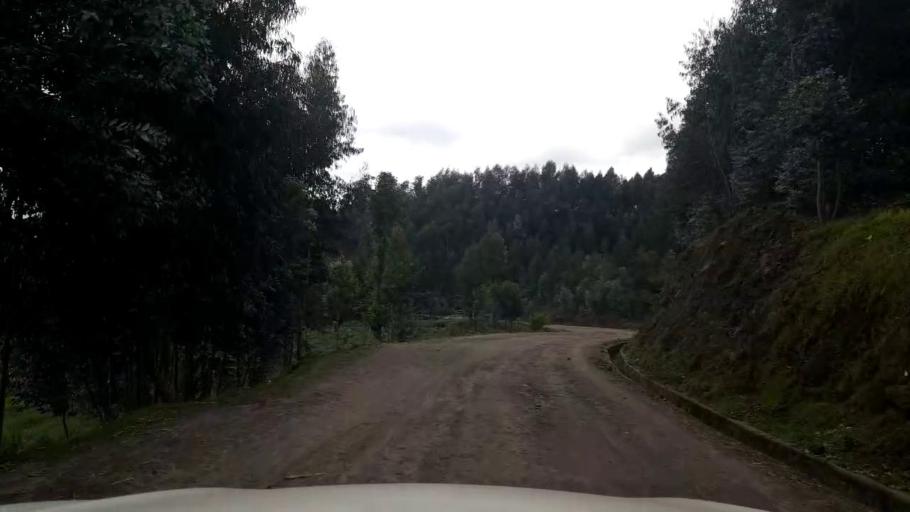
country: RW
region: Northern Province
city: Musanze
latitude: -1.5289
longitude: 29.5308
